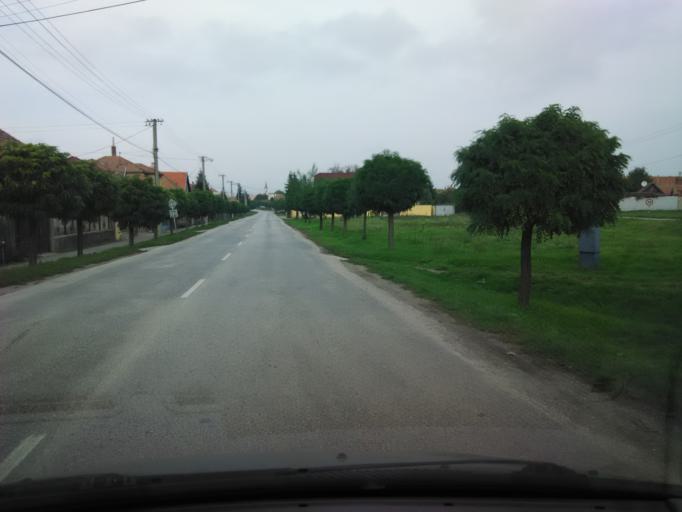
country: SK
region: Nitriansky
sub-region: Okres Nove Zamky
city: Nove Zamky
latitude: 47.9857
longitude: 18.2662
